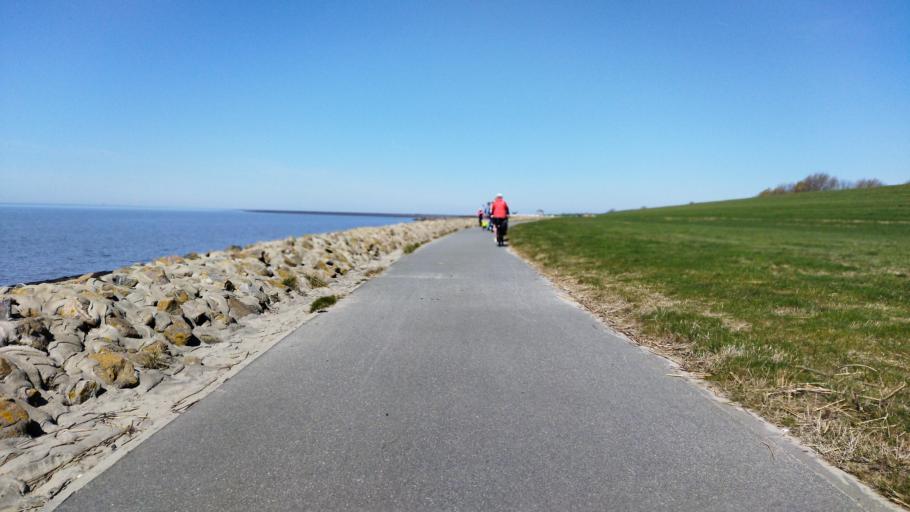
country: DE
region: Lower Saxony
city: Wremen
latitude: 53.6272
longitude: 8.5053
